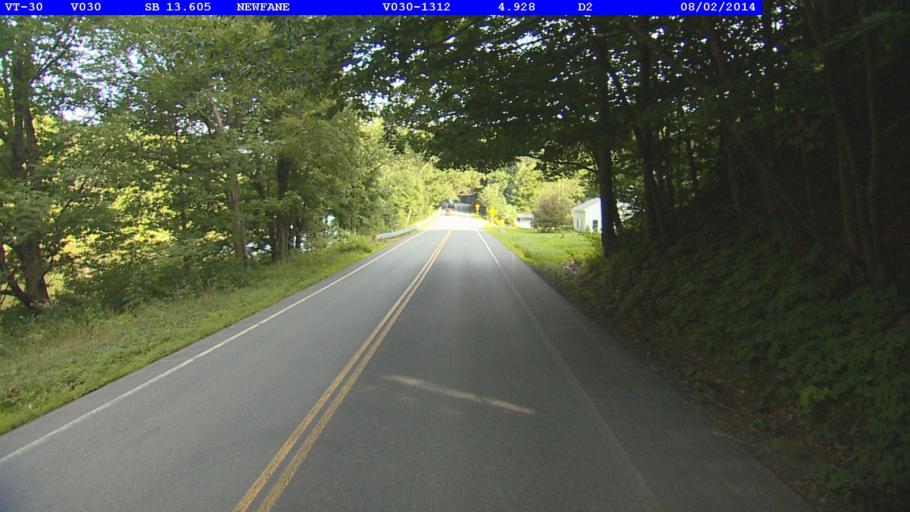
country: US
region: Vermont
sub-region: Windham County
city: Newfane
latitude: 43.0110
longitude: -72.6480
